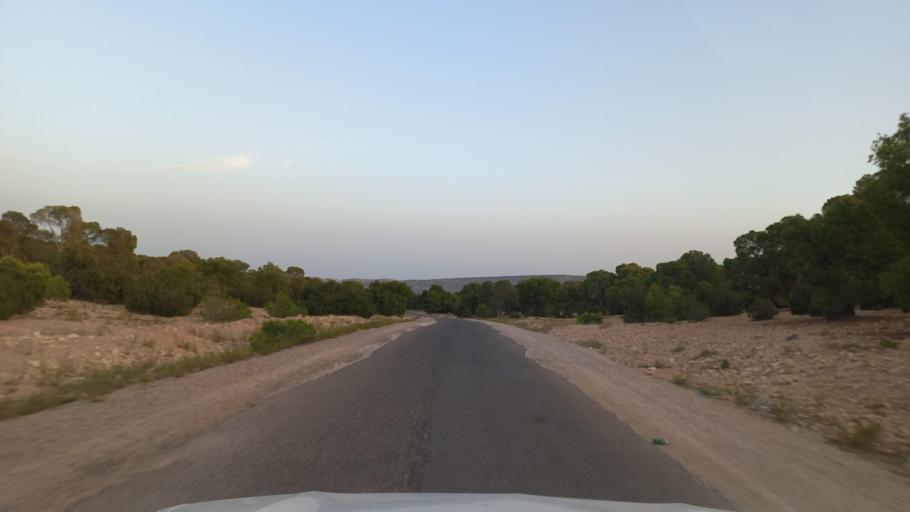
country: TN
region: Al Qasrayn
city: Sbiba
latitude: 35.4246
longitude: 8.9216
